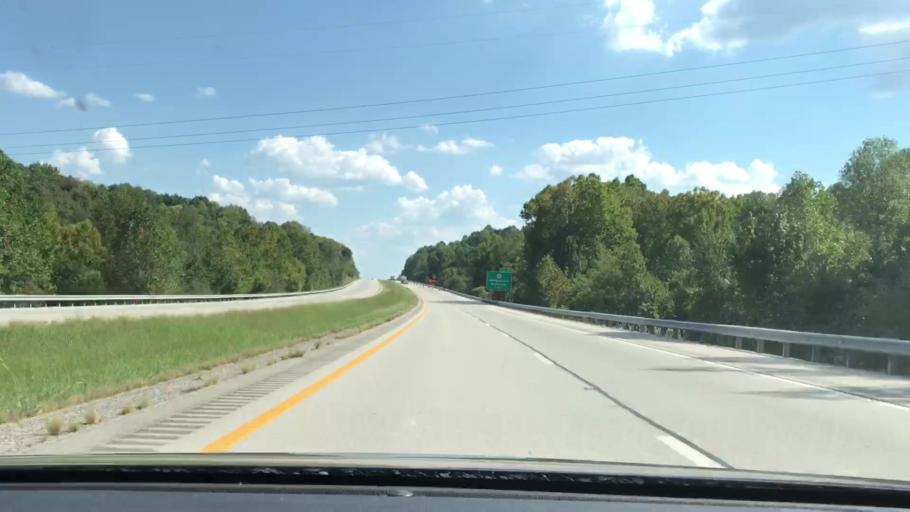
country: US
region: Kentucky
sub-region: Butler County
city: Morgantown
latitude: 37.2313
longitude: -86.7268
